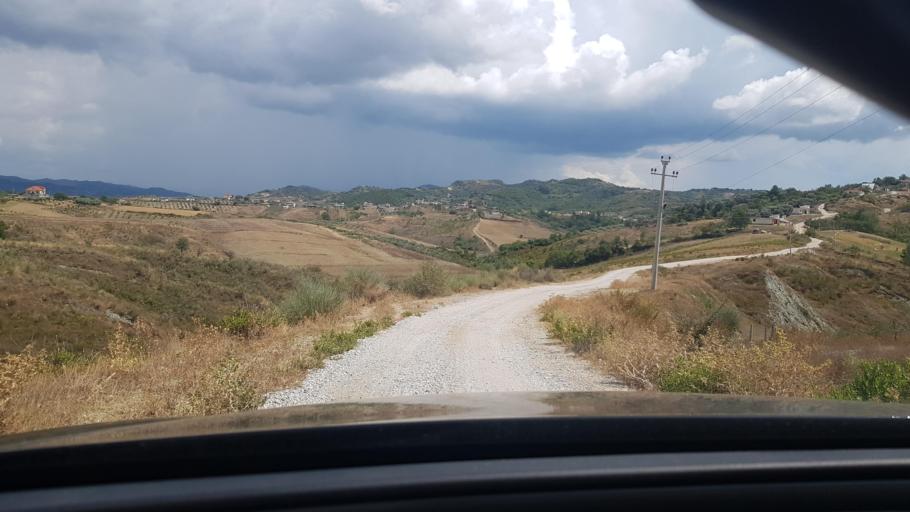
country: AL
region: Durres
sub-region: Rrethi i Durresit
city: Rrashbull
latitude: 41.2936
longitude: 19.5462
